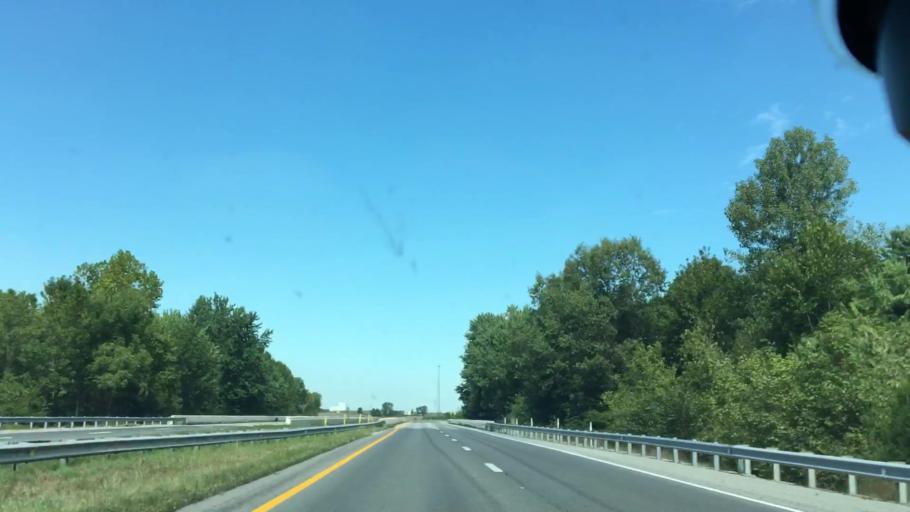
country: US
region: Kentucky
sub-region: Webster County
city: Sebree
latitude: 37.5643
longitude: -87.4781
